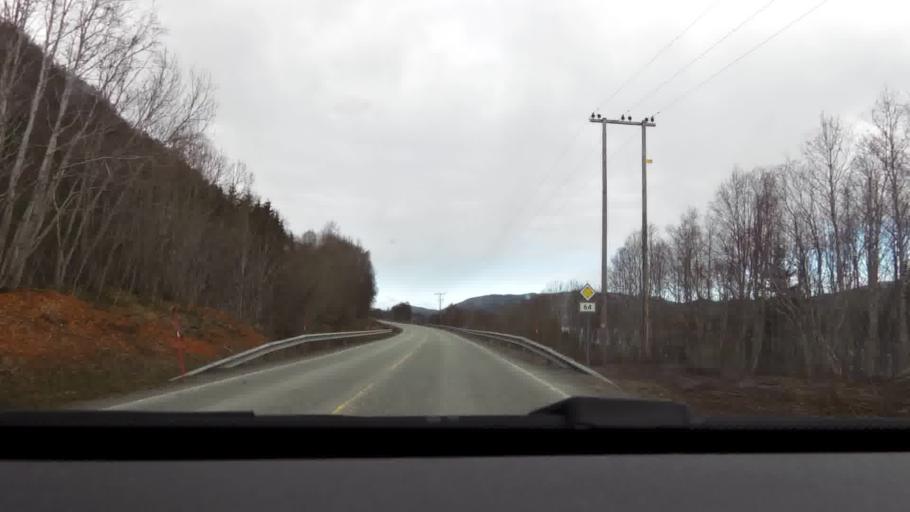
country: NO
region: More og Romsdal
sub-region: Kristiansund
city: Rensvik
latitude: 63.1094
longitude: 7.7803
